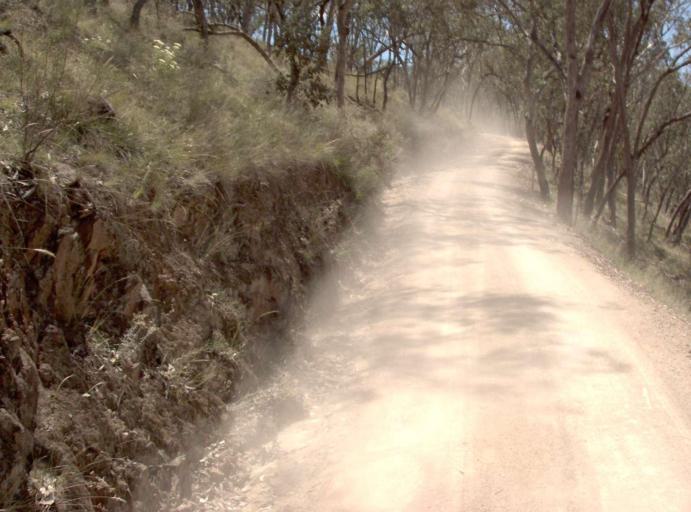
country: AU
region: New South Wales
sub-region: Snowy River
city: Jindabyne
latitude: -37.0900
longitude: 148.3654
